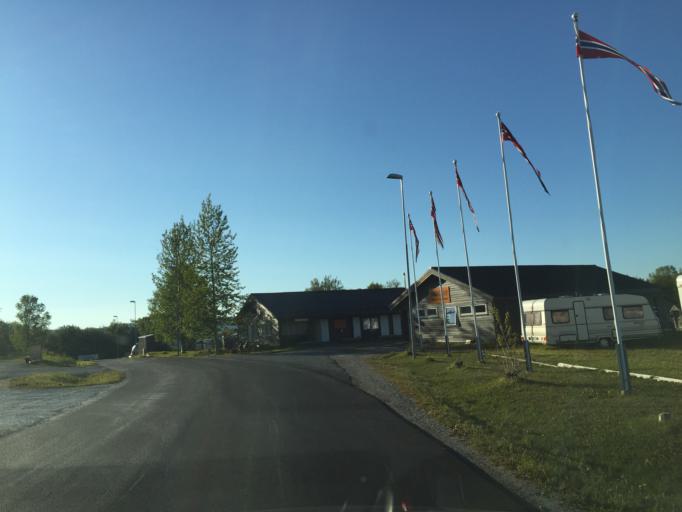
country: NO
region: Nordland
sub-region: Bodo
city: Loding
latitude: 67.2351
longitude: 14.6212
